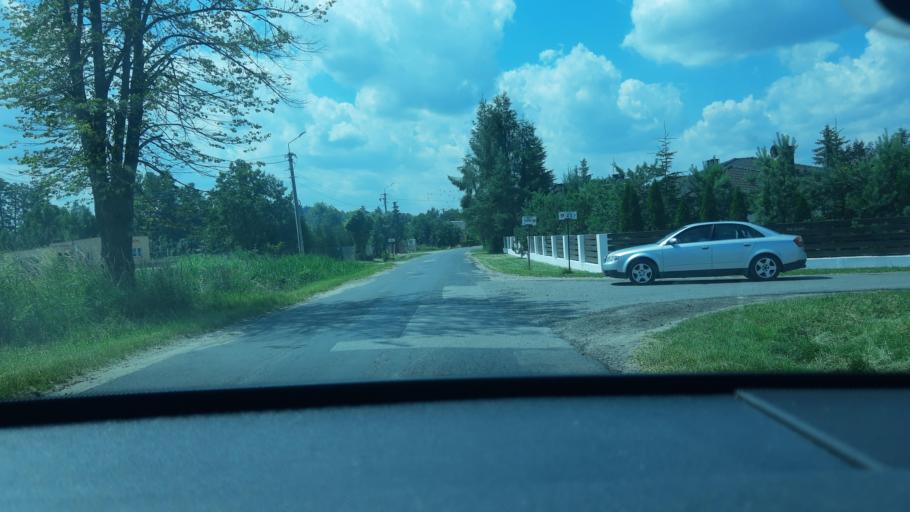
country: PL
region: Lodz Voivodeship
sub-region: Powiat sieradzki
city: Sieradz
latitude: 51.5487
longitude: 18.7570
